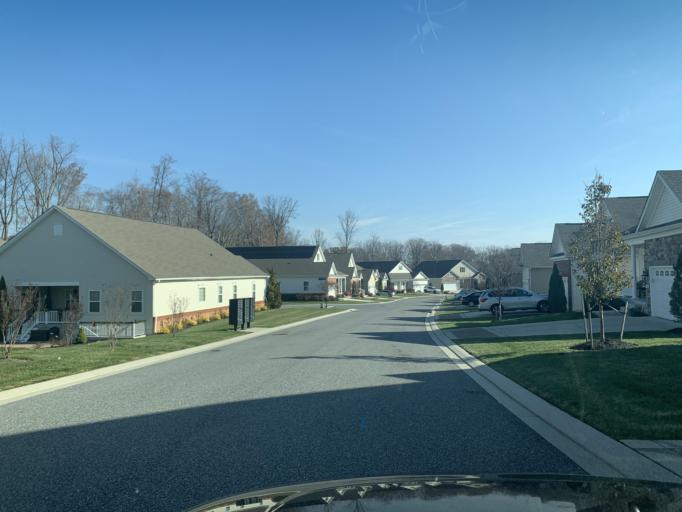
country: US
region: Maryland
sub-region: Harford County
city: Havre de Grace
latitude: 39.5433
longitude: -76.1189
